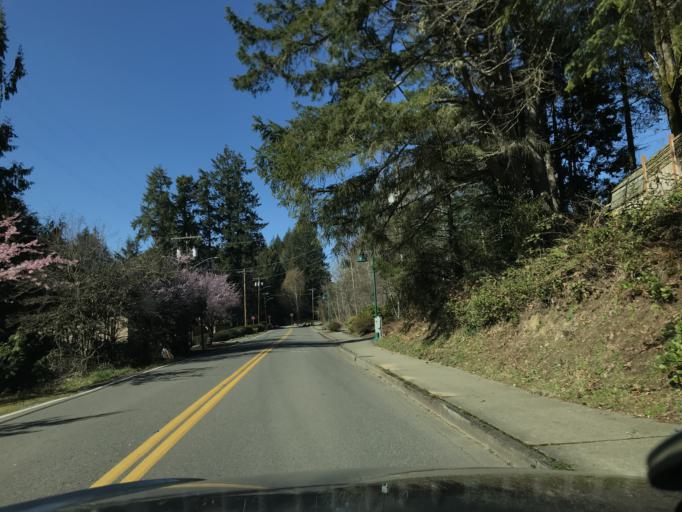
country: US
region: Washington
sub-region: Pierce County
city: Gig Harbor
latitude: 47.3409
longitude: -122.5954
